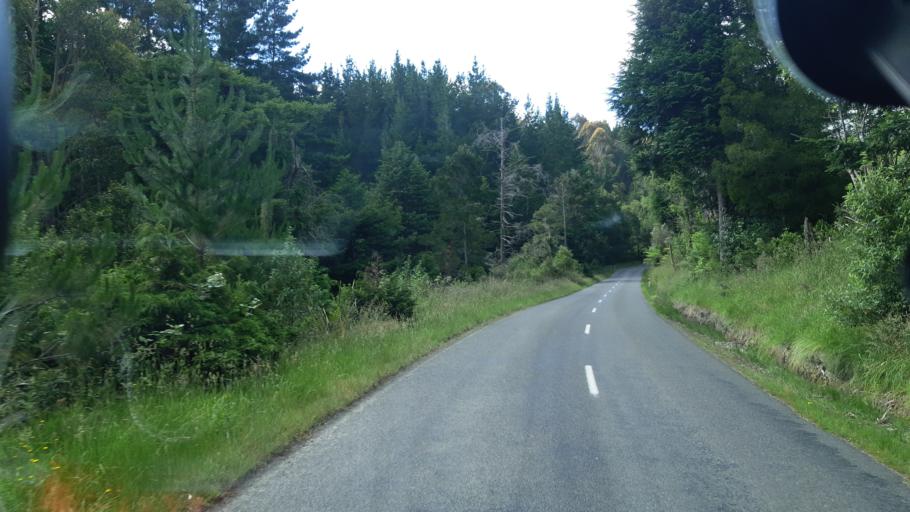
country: NZ
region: Manawatu-Wanganui
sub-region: Rangitikei District
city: Bulls
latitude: -39.9182
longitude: 175.5551
